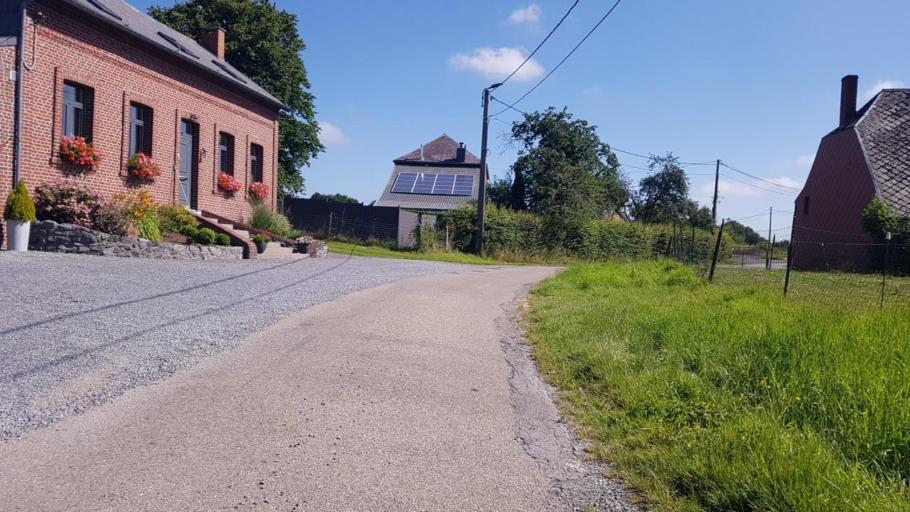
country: BE
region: Wallonia
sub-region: Province du Hainaut
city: Momignies
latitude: 50.0084
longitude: 4.1448
